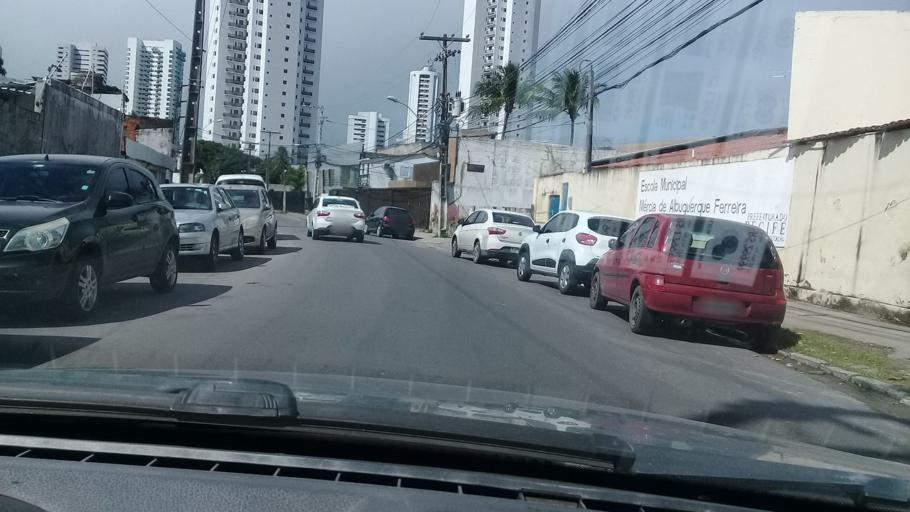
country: BR
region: Pernambuco
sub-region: Recife
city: Recife
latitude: -8.0654
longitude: -34.9065
